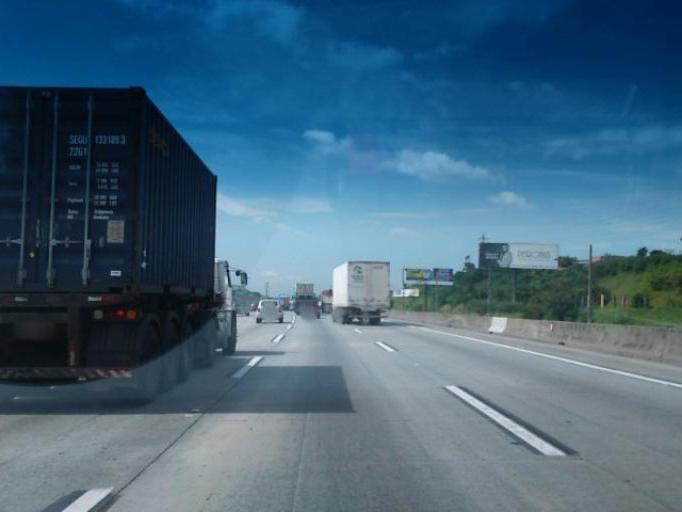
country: BR
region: Sao Paulo
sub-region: Carapicuiba
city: Carapicuiba
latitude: -23.5314
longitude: -46.8181
